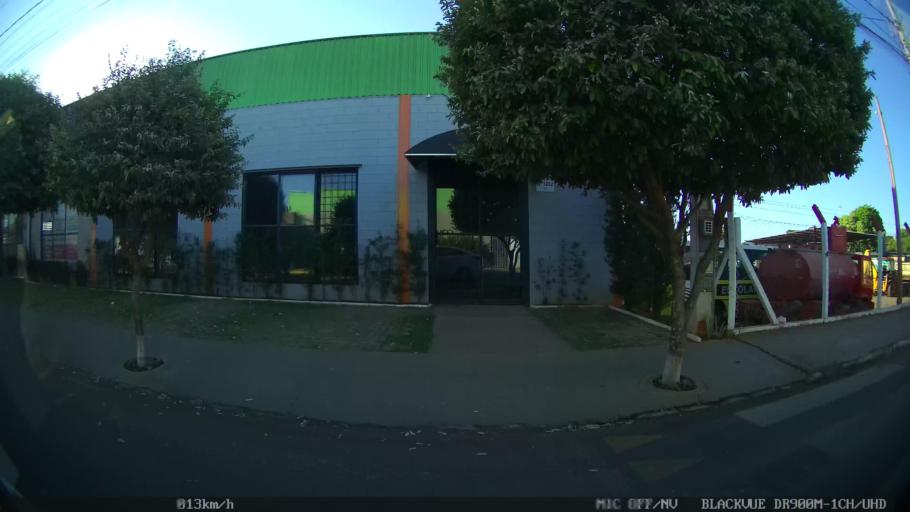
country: BR
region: Sao Paulo
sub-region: Guapiacu
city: Guapiacu
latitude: -20.7945
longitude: -49.2268
